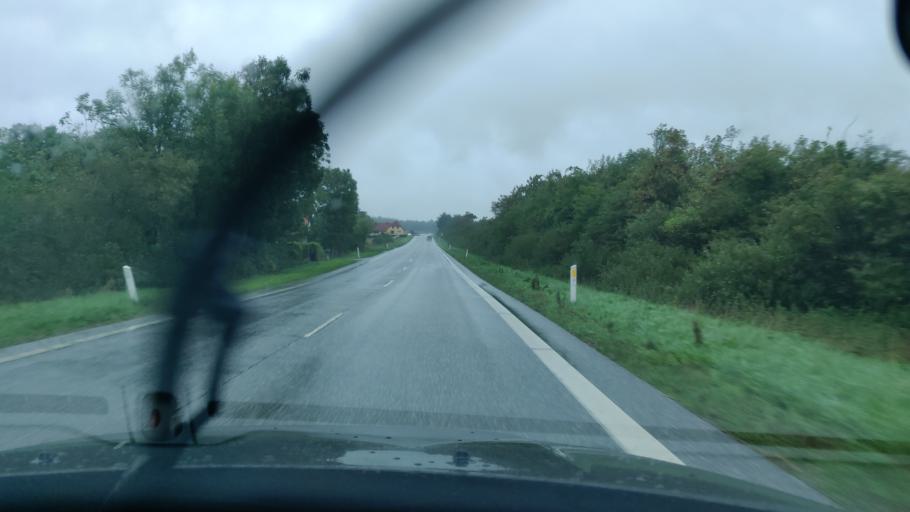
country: DK
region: North Denmark
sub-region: Thisted Kommune
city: Hurup
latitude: 56.8279
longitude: 8.5024
